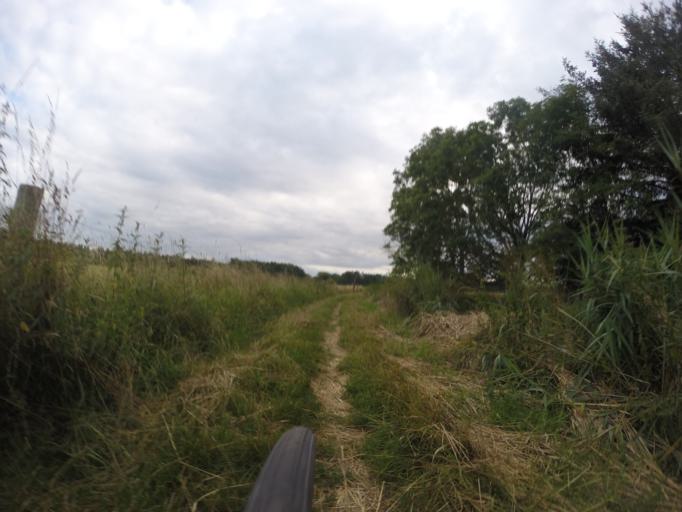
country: DK
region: Capital Region
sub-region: Ballerup Kommune
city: Ballerup
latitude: 55.7064
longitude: 12.3412
